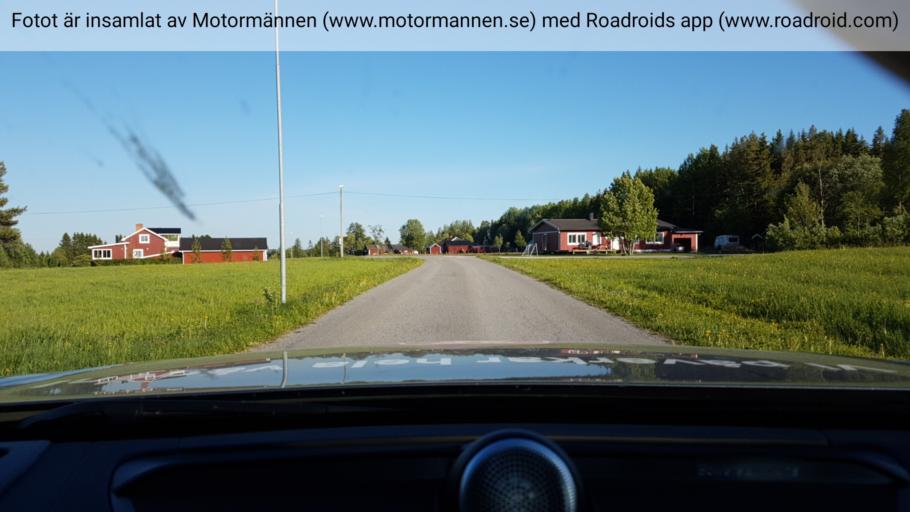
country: SE
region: Jaemtland
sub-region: OEstersunds Kommun
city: Brunflo
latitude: 63.0120
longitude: 14.7136
